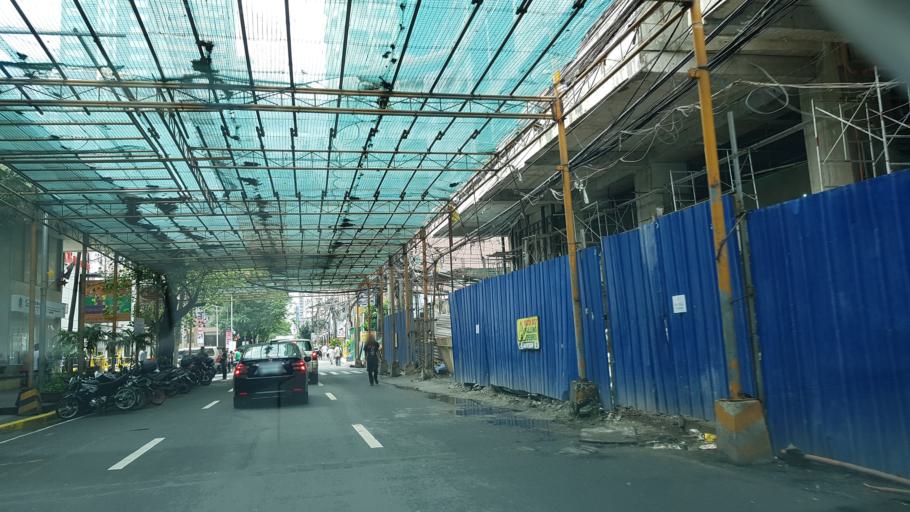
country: PH
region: Metro Manila
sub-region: City of Manila
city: Port Area
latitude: 14.5770
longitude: 120.9823
